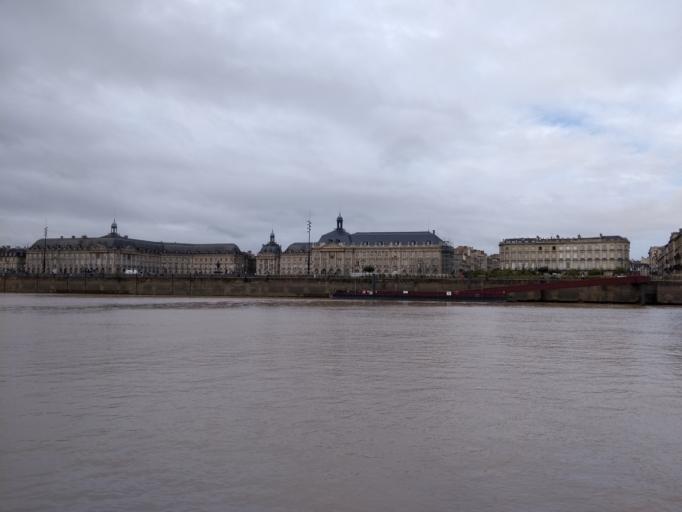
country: FR
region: Aquitaine
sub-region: Departement de la Gironde
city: Bordeaux
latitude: 44.8435
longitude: -0.5676
